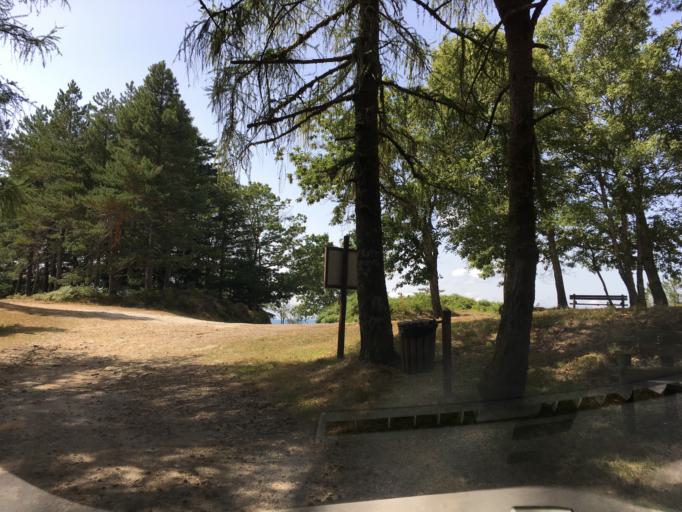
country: PT
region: Braga
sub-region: Celorico de Basto
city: Celorico de Basto
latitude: 41.2769
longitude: -7.9472
